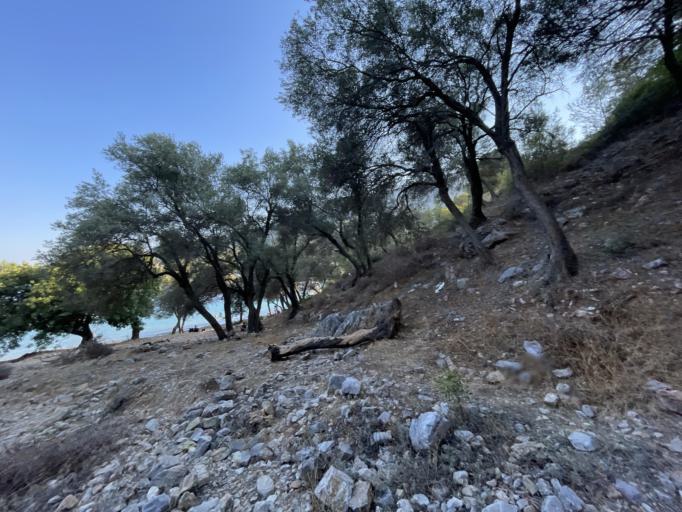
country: TR
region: Mugla
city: Dalaman
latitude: 36.6648
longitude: 28.8539
